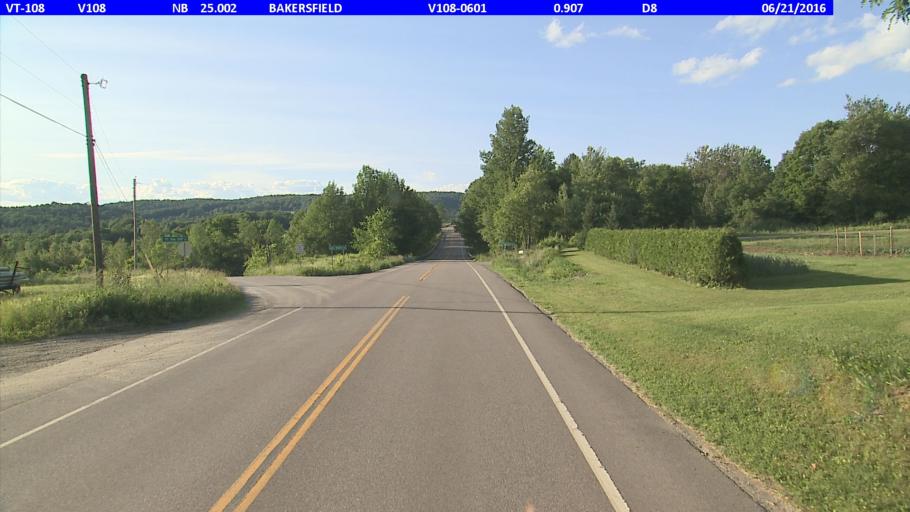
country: US
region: Vermont
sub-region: Franklin County
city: Enosburg Falls
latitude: 44.7462
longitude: -72.8234
